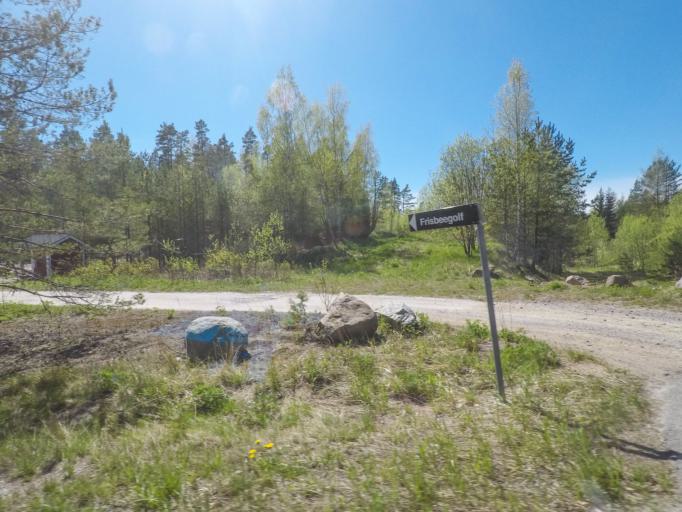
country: FI
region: Uusimaa
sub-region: Helsinki
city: Sammatti
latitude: 60.3321
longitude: 23.8115
